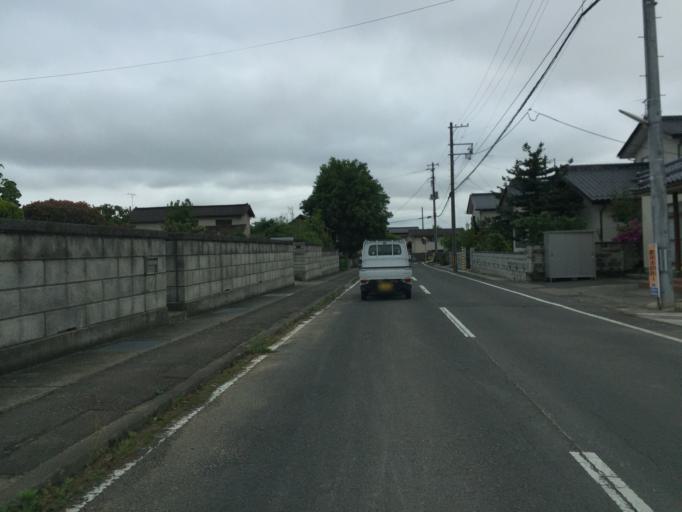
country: JP
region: Fukushima
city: Fukushima-shi
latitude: 37.7688
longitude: 140.3862
